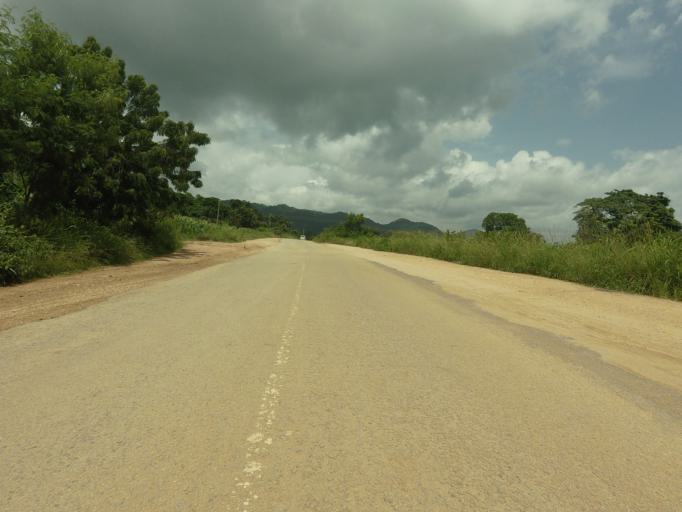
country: GH
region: Volta
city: Ho
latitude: 6.7001
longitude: 0.3351
